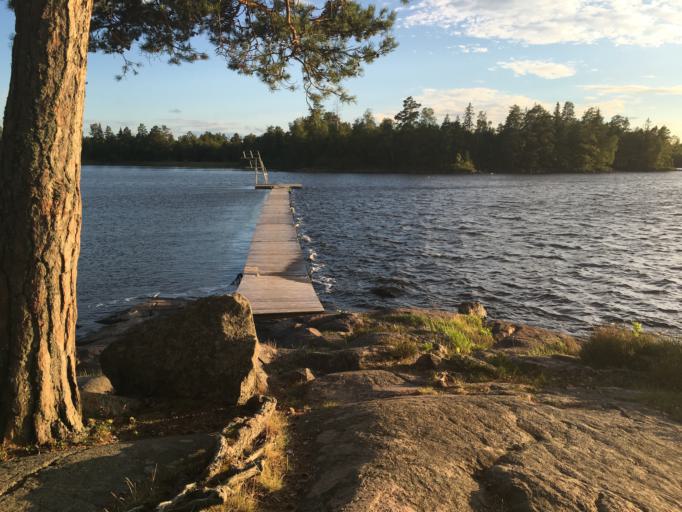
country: SE
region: Kalmar
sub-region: Nybro Kommun
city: Nybro
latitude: 56.9401
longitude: 15.9055
